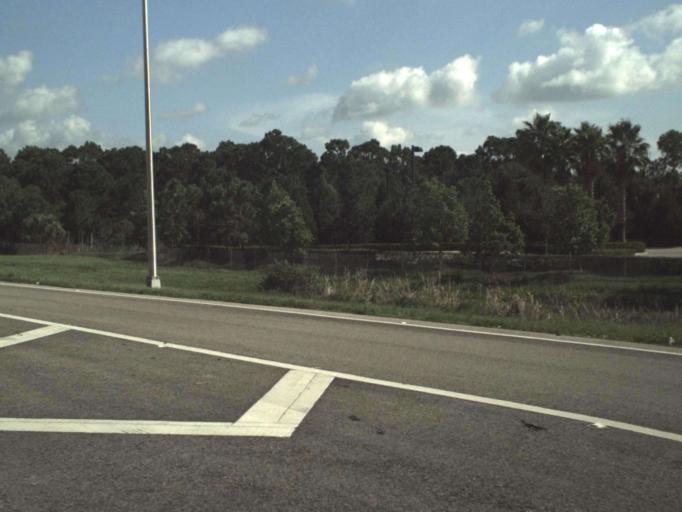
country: US
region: Florida
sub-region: Palm Beach County
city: Palm Beach Gardens
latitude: 26.8488
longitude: -80.1076
